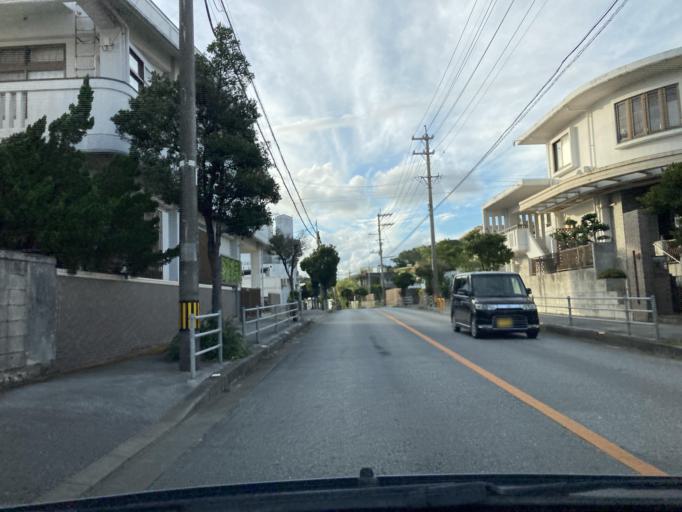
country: JP
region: Okinawa
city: Tomigusuku
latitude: 26.1505
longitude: 127.7089
